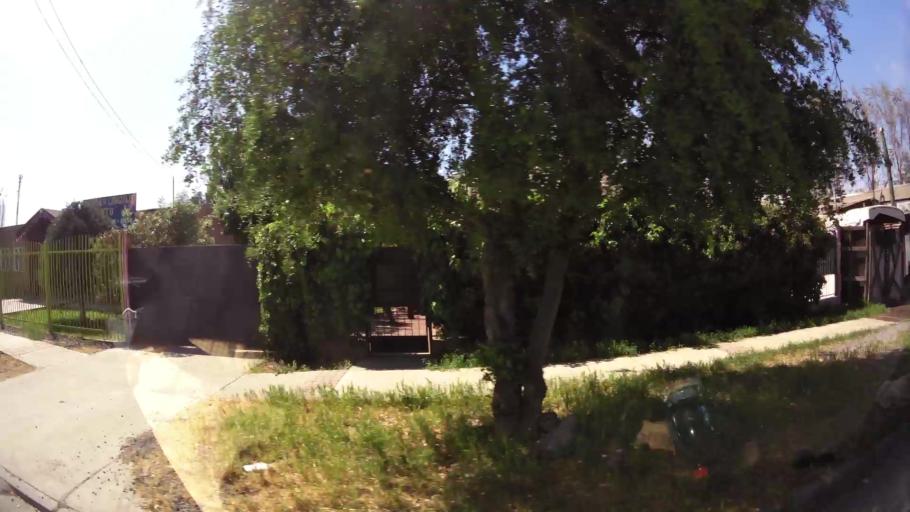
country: CL
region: Santiago Metropolitan
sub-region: Provincia de Talagante
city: Talagante
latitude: -33.6543
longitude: -70.9225
